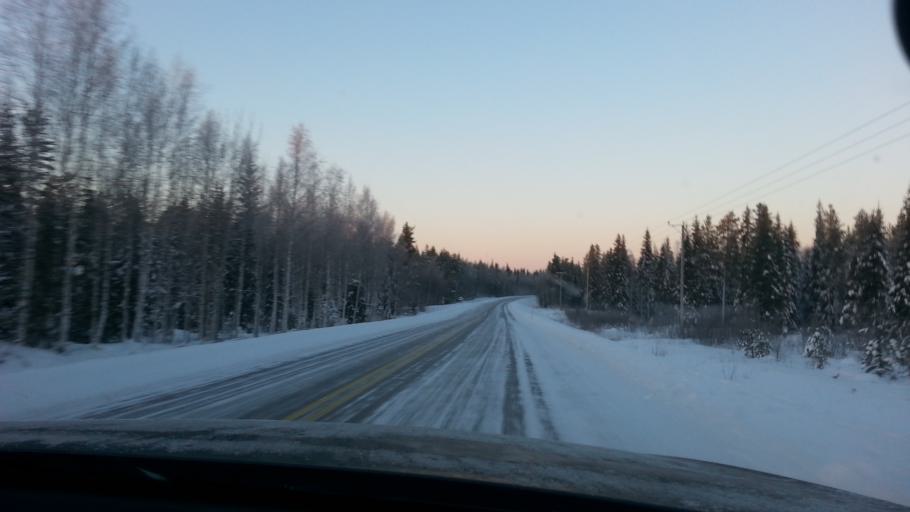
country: FI
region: Lapland
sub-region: Rovaniemi
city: Rovaniemi
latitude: 66.7889
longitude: 25.4396
